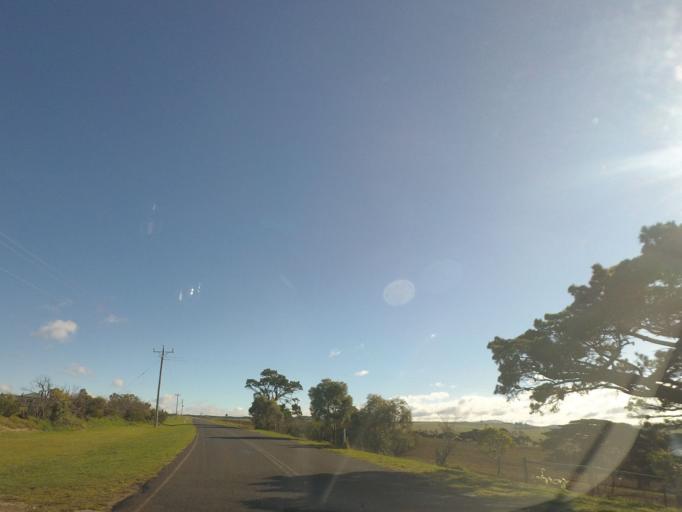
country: AU
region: Victoria
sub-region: Moorabool
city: Bacchus Marsh
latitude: -37.6545
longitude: 144.3730
